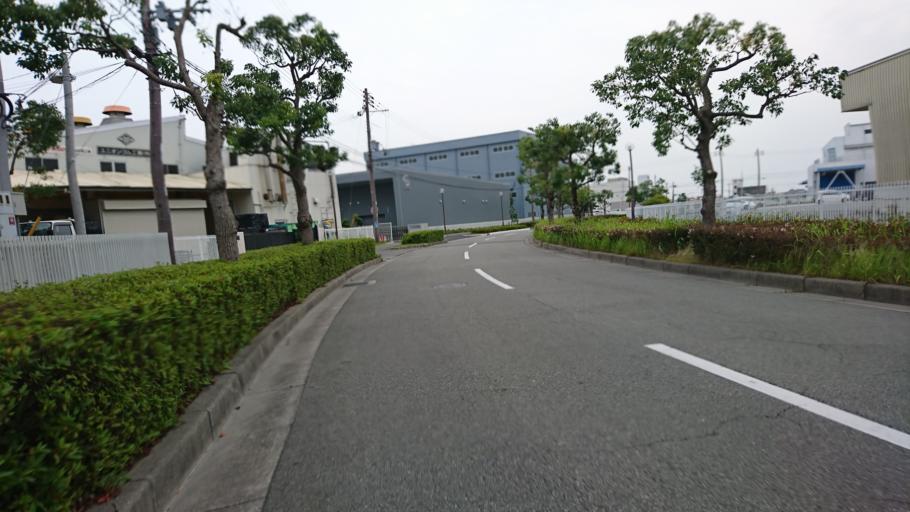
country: JP
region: Hyogo
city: Kakogawacho-honmachi
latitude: 34.7367
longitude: 134.8856
